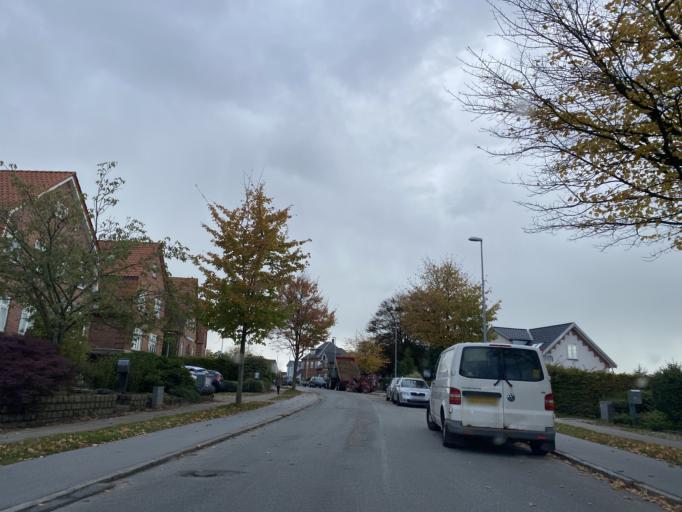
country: DK
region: South Denmark
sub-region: Haderslev Kommune
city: Haderslev
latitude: 55.2455
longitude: 9.4988
